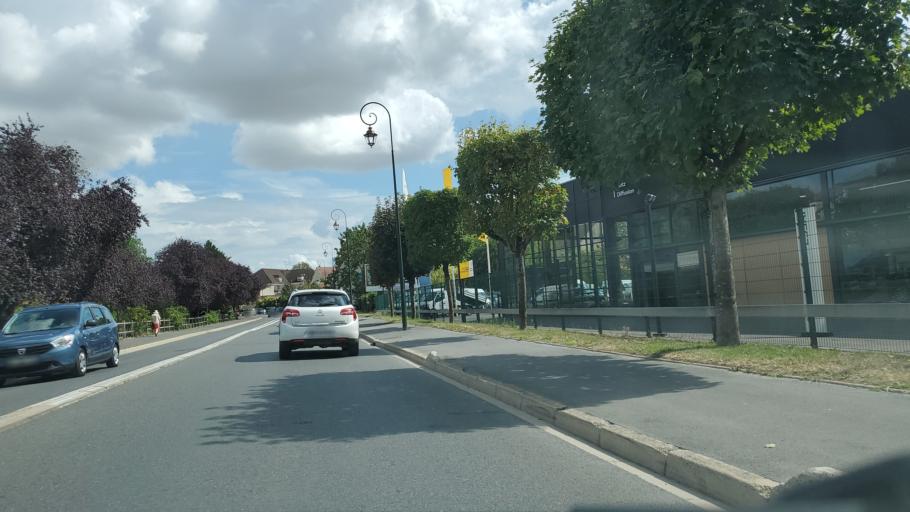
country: FR
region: Ile-de-France
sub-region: Departement de Seine-et-Marne
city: Coulommiers
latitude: 48.8098
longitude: 3.0805
